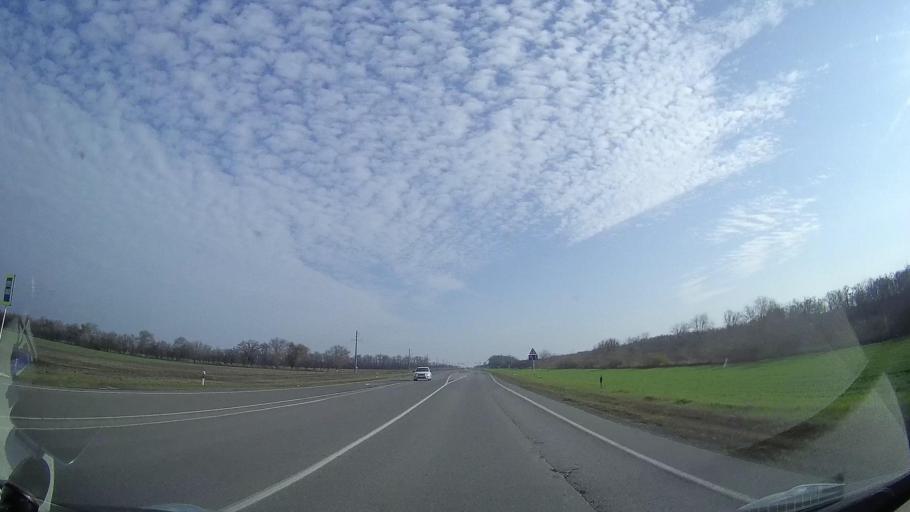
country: RU
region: Rostov
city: Gigant
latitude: 46.5261
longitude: 41.2282
